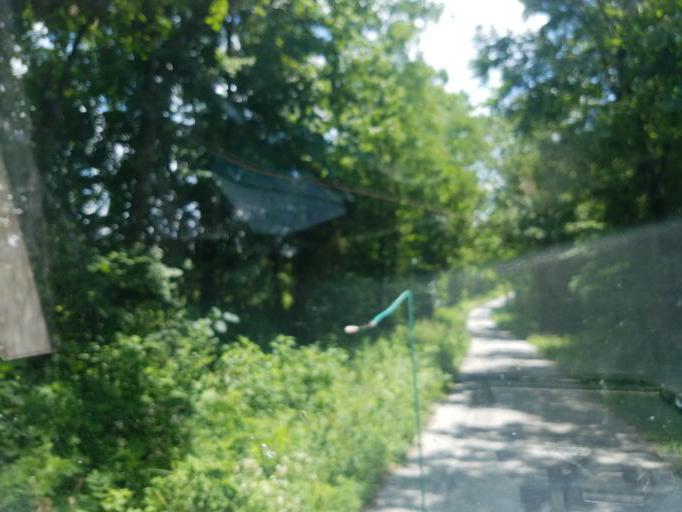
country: US
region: Kentucky
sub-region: Grayson County
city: Leitchfield
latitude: 37.4812
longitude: -86.4643
